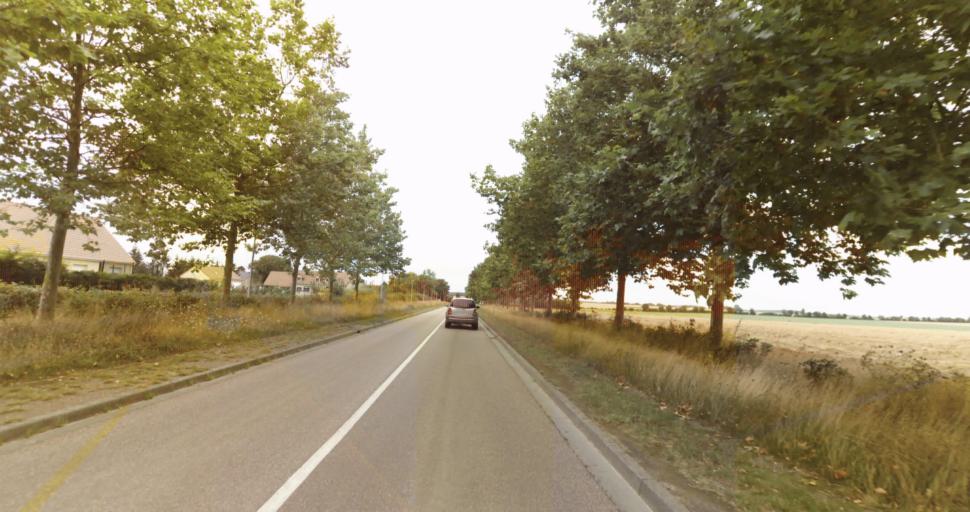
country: FR
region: Haute-Normandie
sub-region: Departement de l'Eure
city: Marcilly-sur-Eure
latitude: 48.9108
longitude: 1.2819
